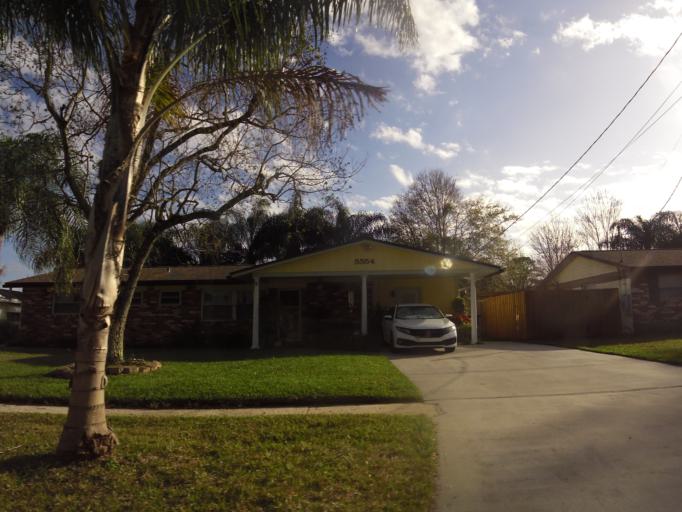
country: US
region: Florida
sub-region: Duval County
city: Jacksonville
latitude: 30.2859
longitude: -81.6078
